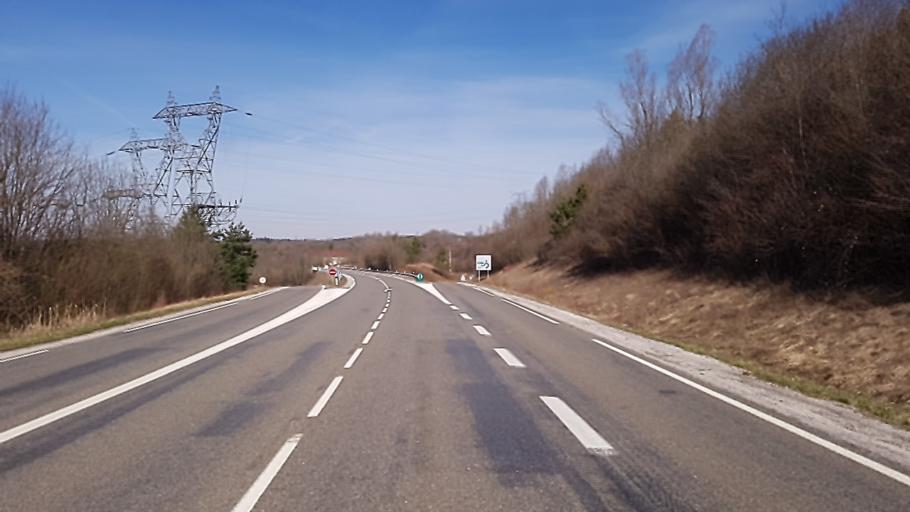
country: FR
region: Franche-Comte
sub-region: Departement du Jura
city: Champagnole
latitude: 46.7583
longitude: 5.9095
